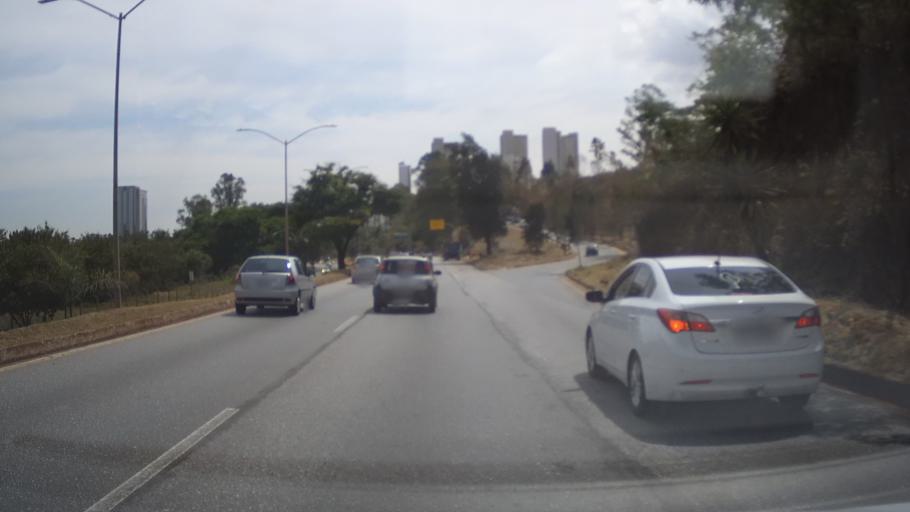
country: BR
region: Minas Gerais
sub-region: Belo Horizonte
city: Belo Horizonte
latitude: -19.9835
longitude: -43.9508
